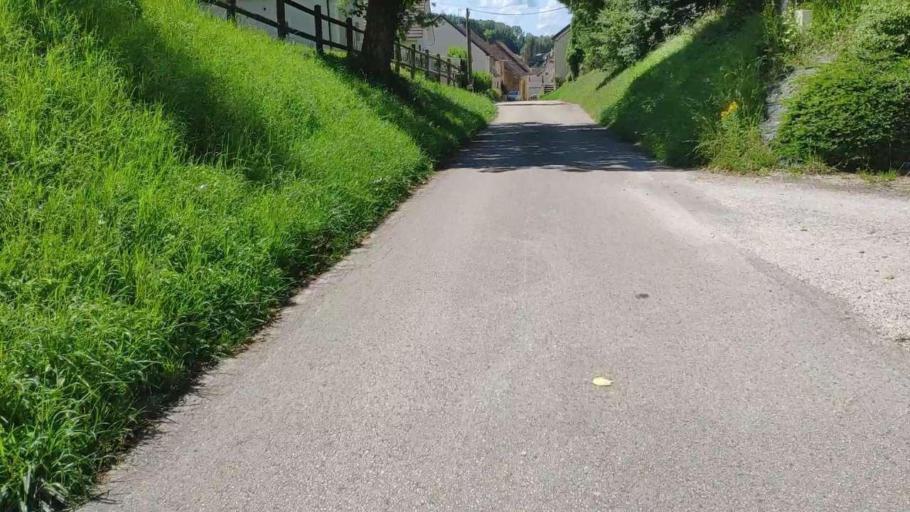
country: FR
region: Franche-Comte
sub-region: Departement du Jura
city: Bletterans
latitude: 46.8307
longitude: 5.5649
